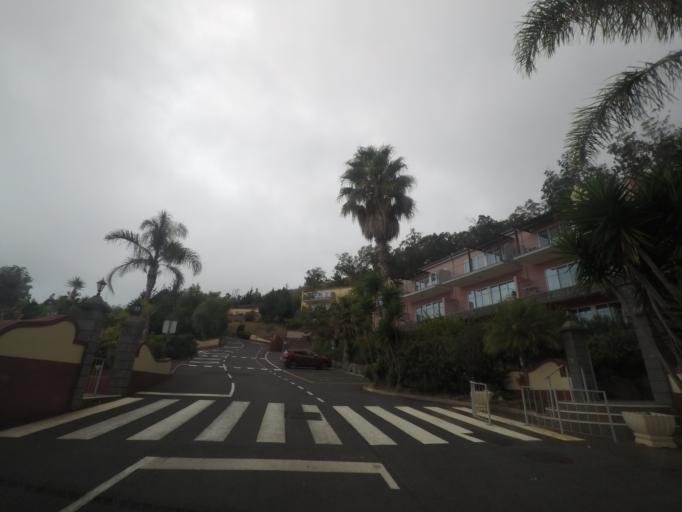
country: PT
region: Madeira
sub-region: Ribeira Brava
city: Campanario
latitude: 32.6583
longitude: -17.0034
